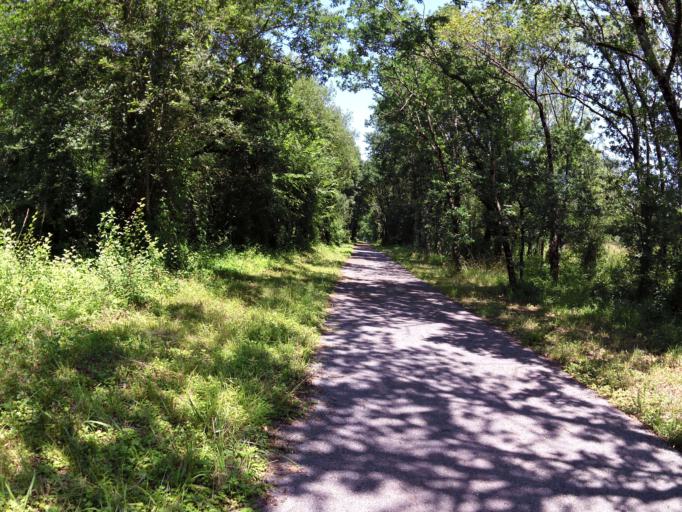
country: FR
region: Aquitaine
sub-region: Departement des Pyrenees-Atlantiques
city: Sauveterre-de-Bearn
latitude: 43.4424
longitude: -0.9946
